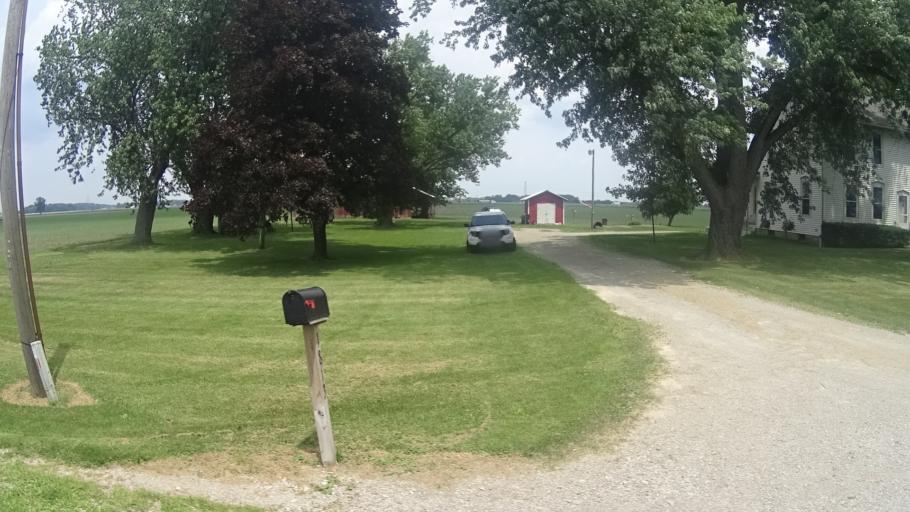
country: US
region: Ohio
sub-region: Erie County
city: Milan
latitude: 41.3228
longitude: -82.6491
